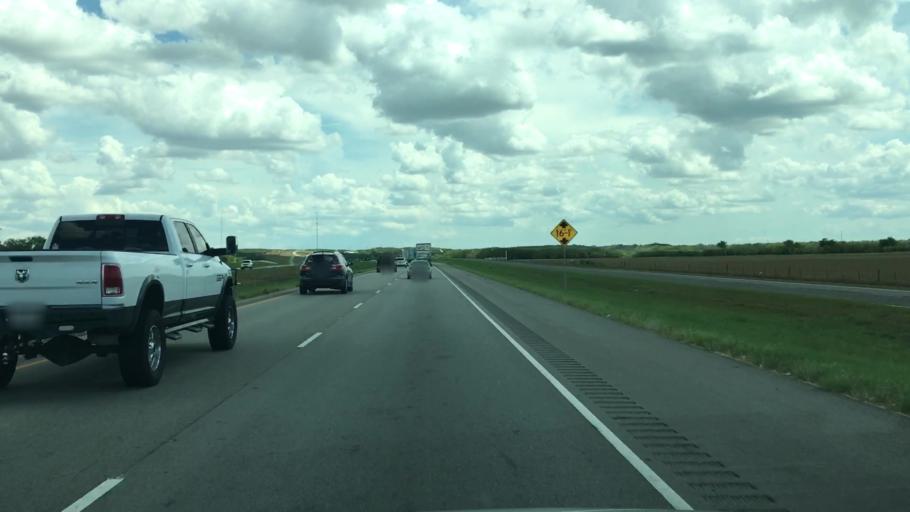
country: US
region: Texas
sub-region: Live Oak County
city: George West
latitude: 28.2693
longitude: -97.9414
